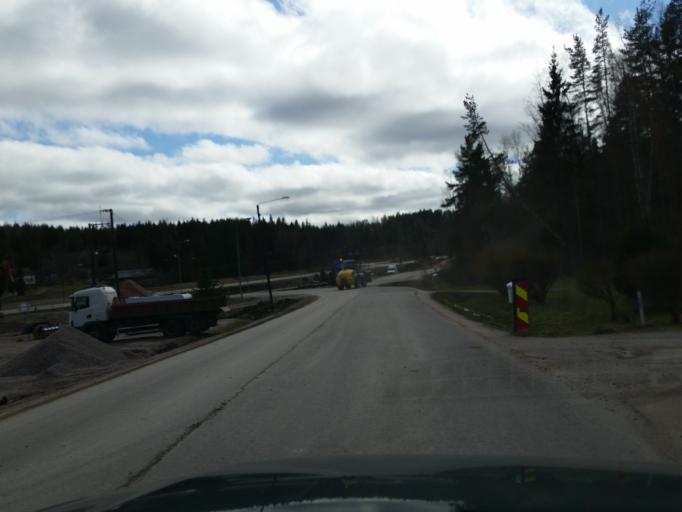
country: FI
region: Uusimaa
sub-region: Helsinki
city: Vihti
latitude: 60.3993
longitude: 24.3296
